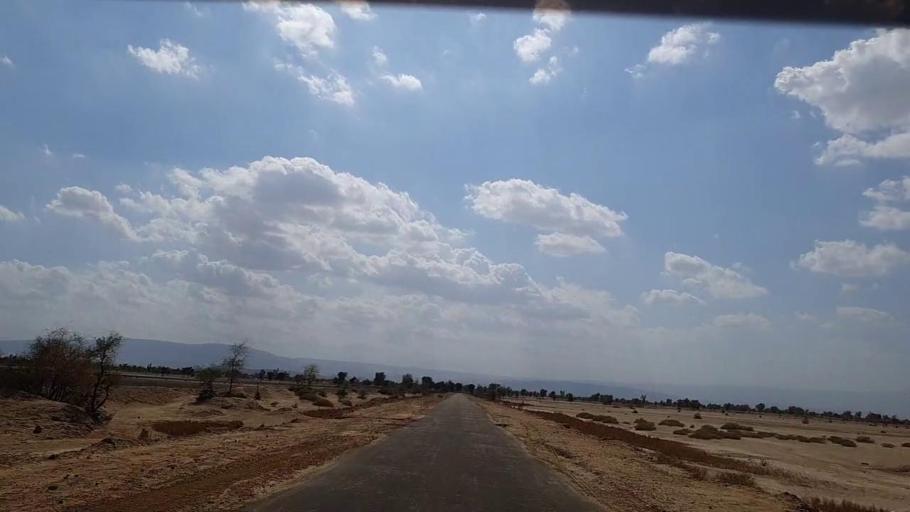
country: PK
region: Sindh
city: Johi
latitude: 26.5222
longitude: 67.4955
